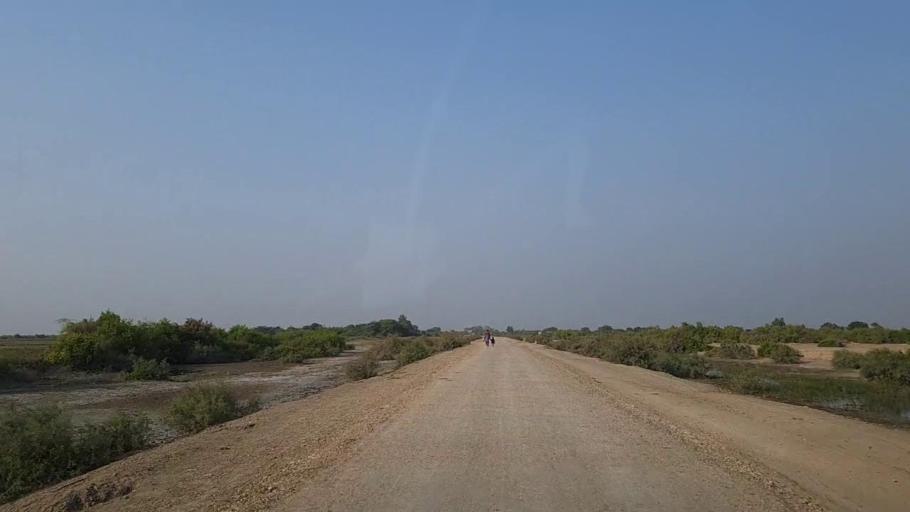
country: PK
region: Sindh
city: Mirpur Sakro
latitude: 24.6402
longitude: 67.7675
